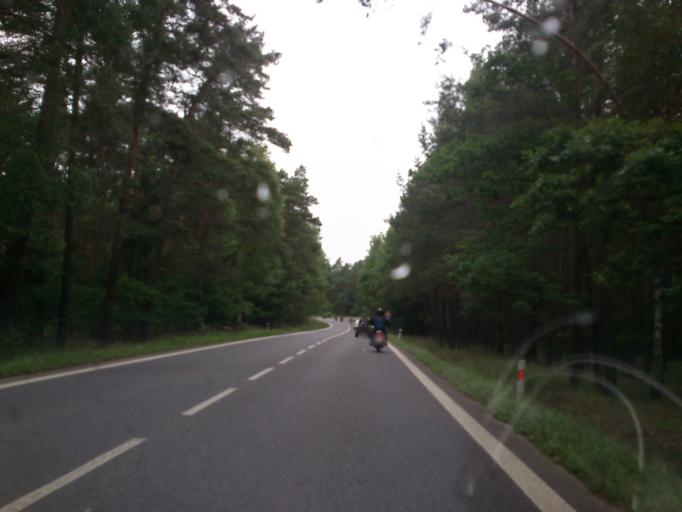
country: CZ
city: Doksy
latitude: 50.5391
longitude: 14.6811
